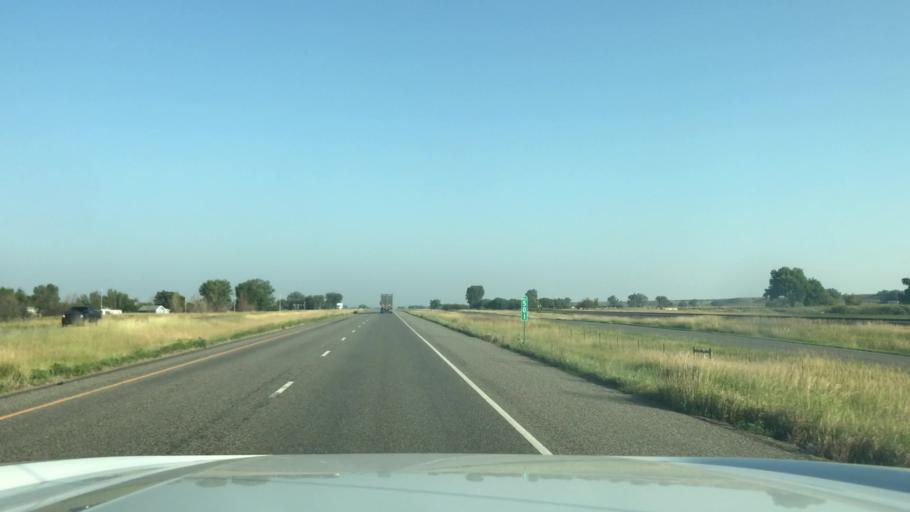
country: US
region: Montana
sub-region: Big Horn County
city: Hardin
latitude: 45.7082
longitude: -107.5311
